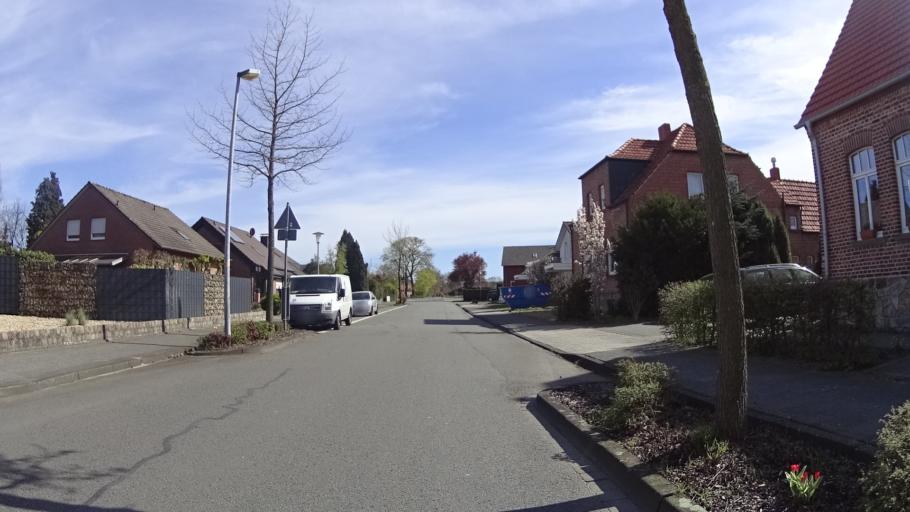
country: DE
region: North Rhine-Westphalia
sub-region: Regierungsbezirk Munster
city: Dreierwalde
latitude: 52.2755
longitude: 7.4792
